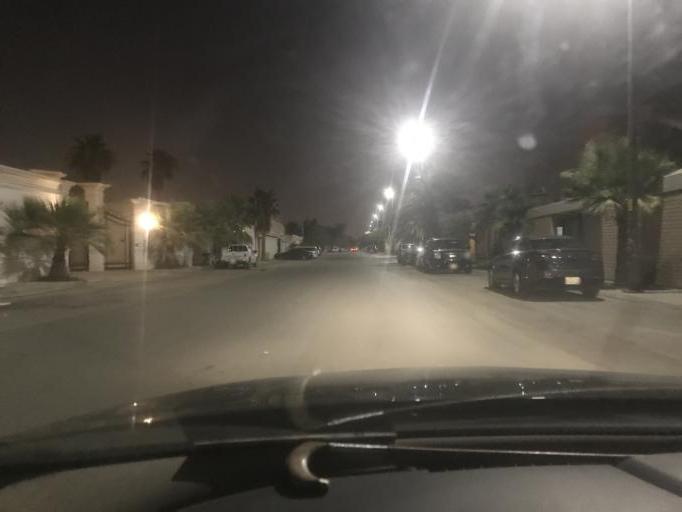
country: SA
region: Ar Riyad
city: Riyadh
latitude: 24.7311
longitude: 46.7795
